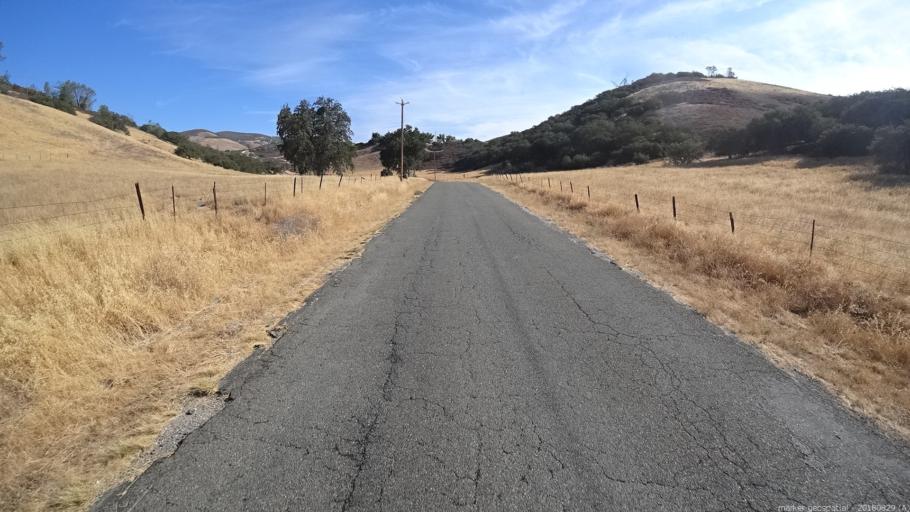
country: US
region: California
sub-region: Monterey County
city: King City
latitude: 35.9785
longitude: -121.0815
